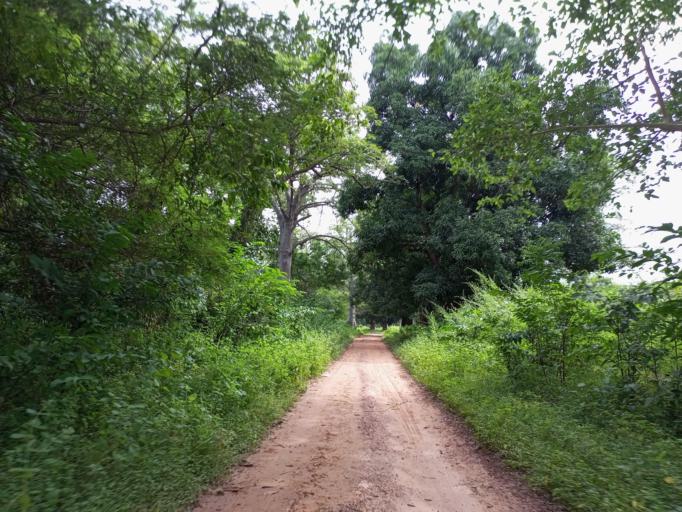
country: GW
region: Oio
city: Farim
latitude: 12.4451
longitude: -15.3174
